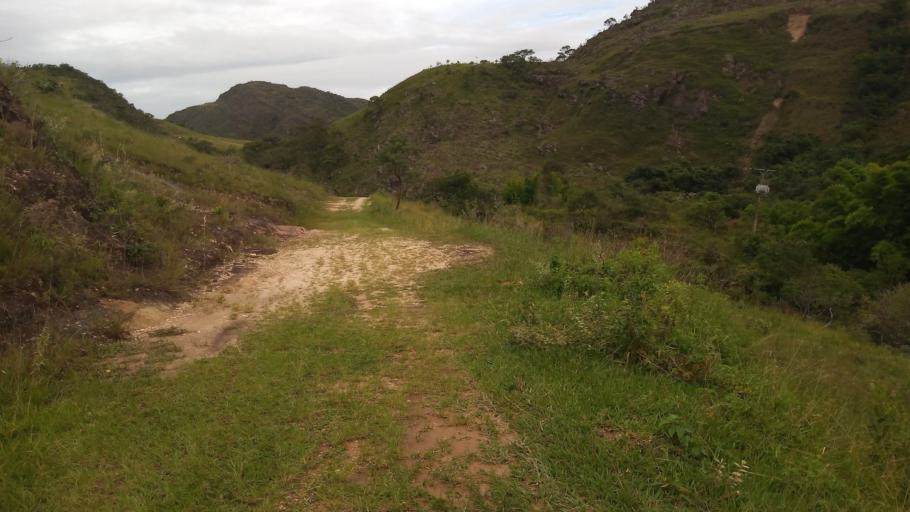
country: BR
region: Minas Gerais
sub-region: Sao Joao Del Rei
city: Sao Joao del Rei
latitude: -21.1258
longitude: -44.2693
